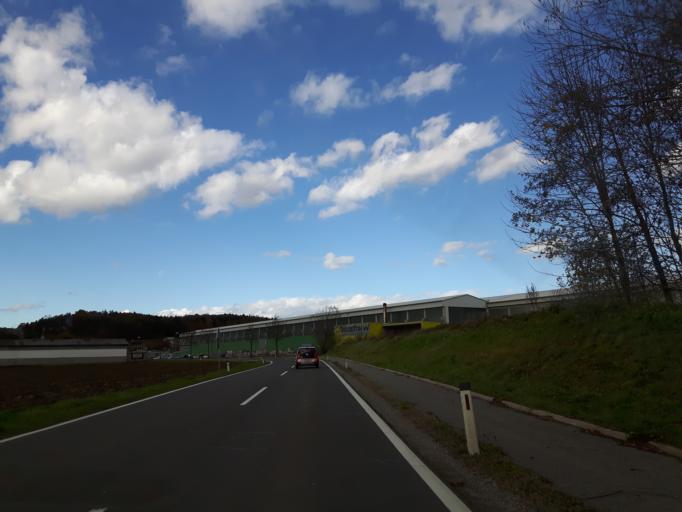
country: AT
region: Styria
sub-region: Politischer Bezirk Suedoststeiermark
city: Kirchbach in Steiermark
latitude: 46.9121
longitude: 15.6783
